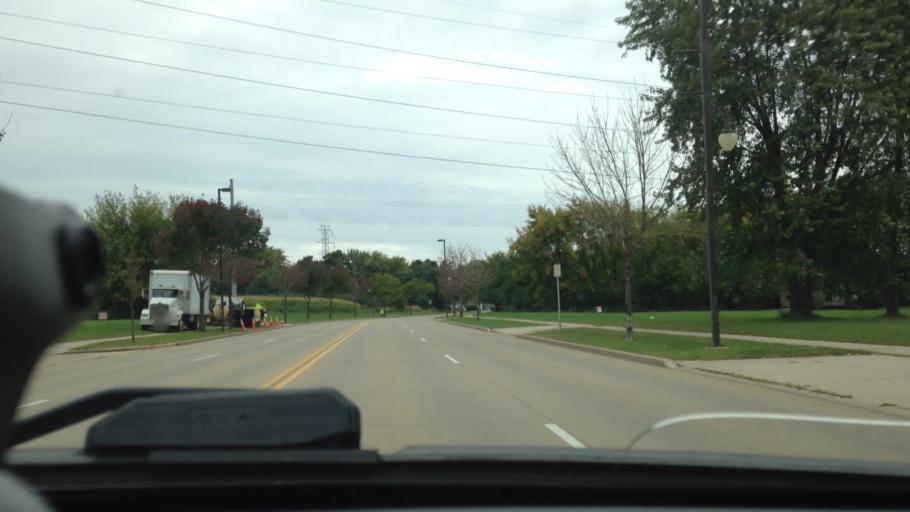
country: US
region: Wisconsin
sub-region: Fond du Lac County
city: North Fond du Lac
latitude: 43.7970
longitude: -88.4770
